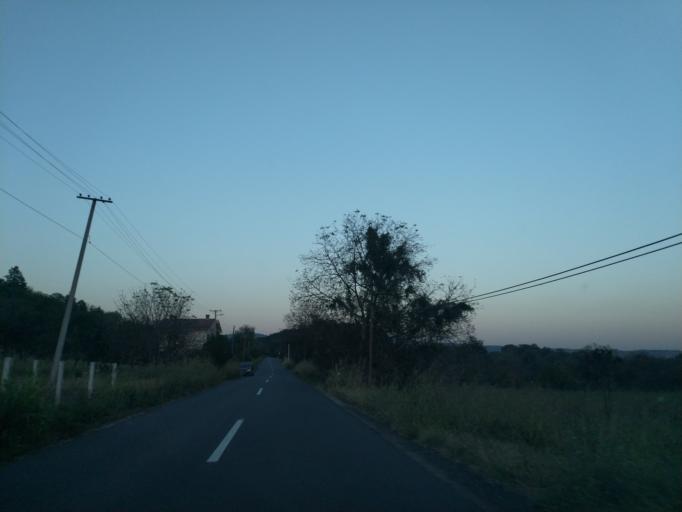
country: RS
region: Central Serbia
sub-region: Rasinski Okrug
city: Krusevac
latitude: 43.6210
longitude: 21.3126
